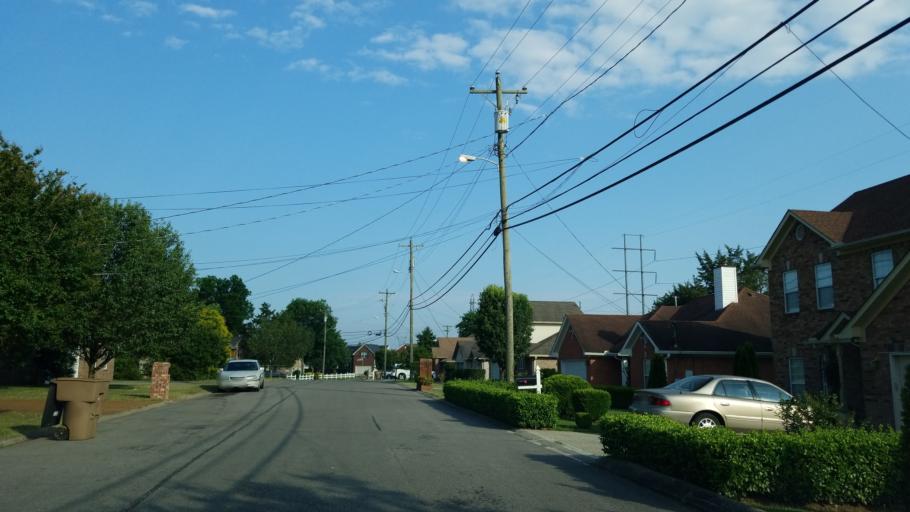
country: US
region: Tennessee
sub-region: Rutherford County
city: La Vergne
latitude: 36.0286
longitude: -86.5872
